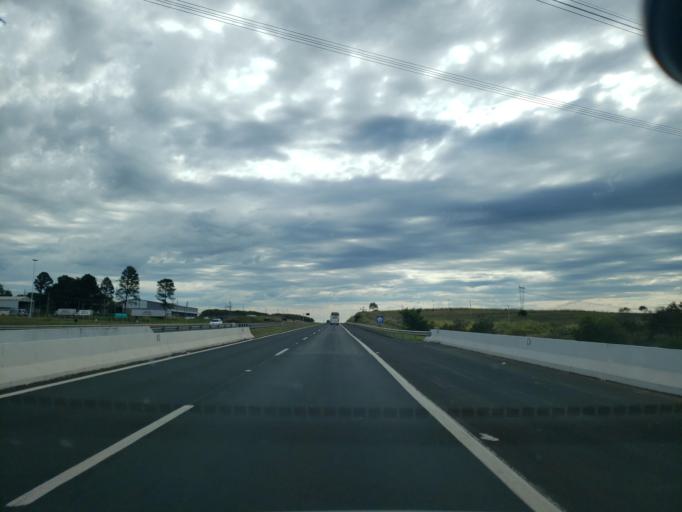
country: BR
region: Sao Paulo
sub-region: Bauru
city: Bauru
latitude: -22.2746
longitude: -49.0947
